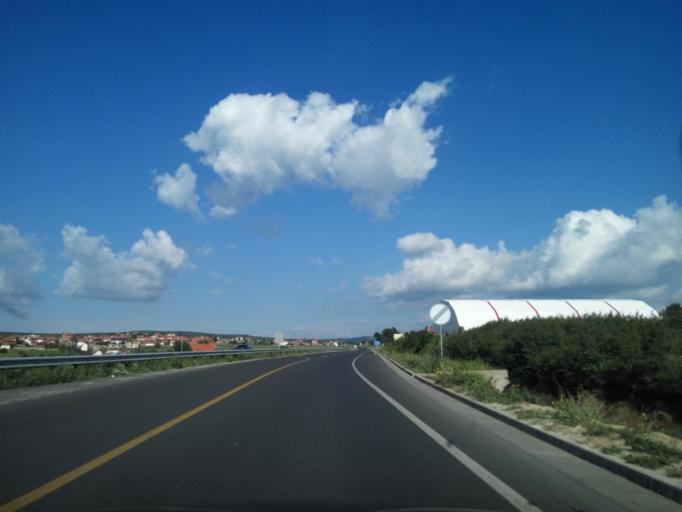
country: XK
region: Prizren
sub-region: Komuna e Malisheves
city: Llazice
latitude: 42.5679
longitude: 20.7429
